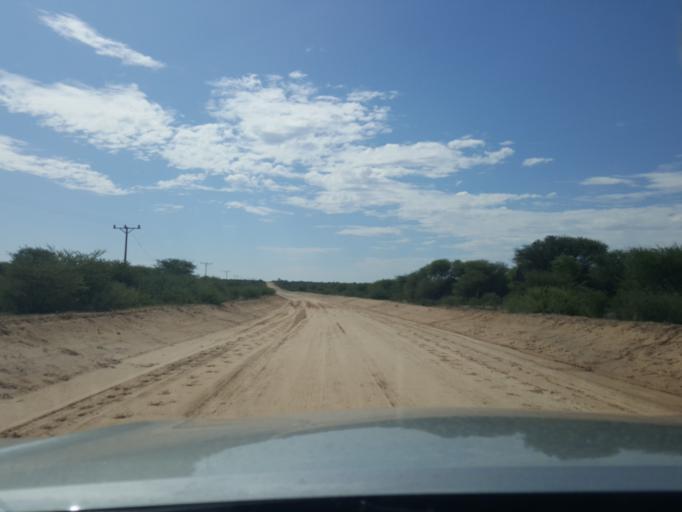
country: BW
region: Kweneng
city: Khudumelapye
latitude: -23.8827
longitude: 24.9091
